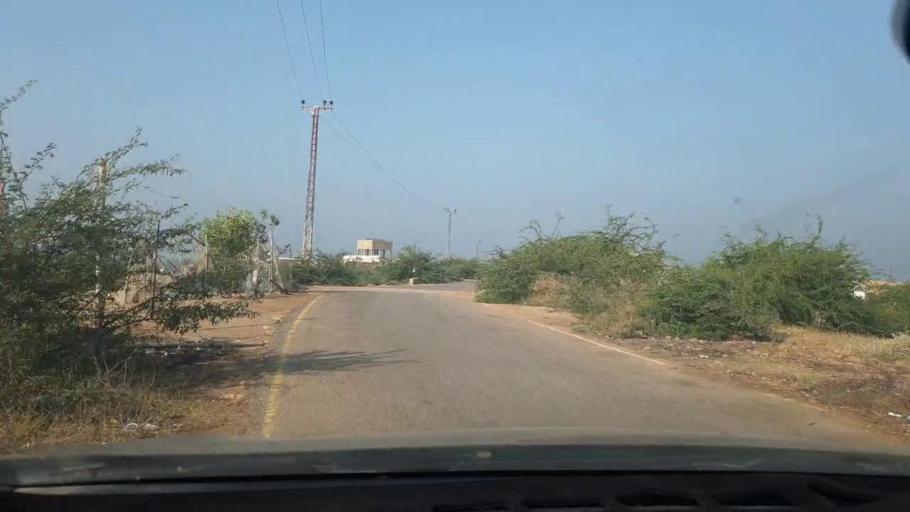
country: PK
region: Balochistan
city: Gadani
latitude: 24.8487
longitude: 66.6654
